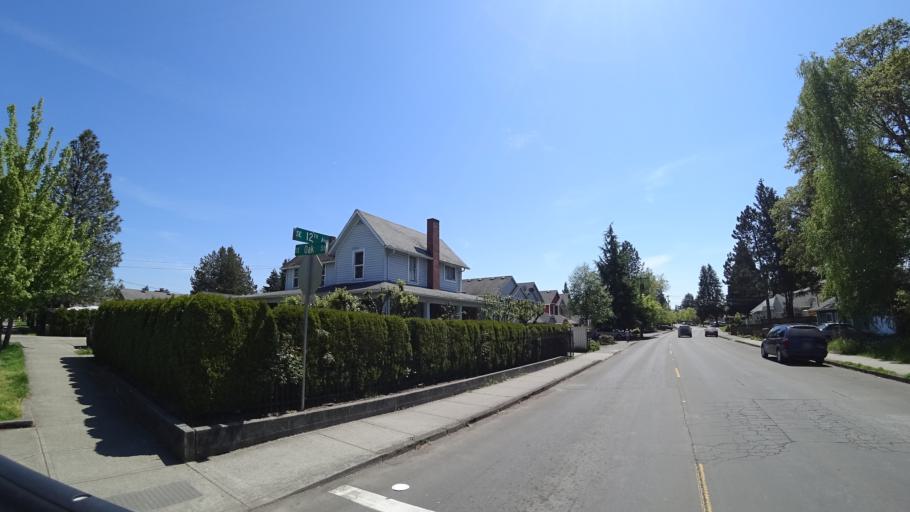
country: US
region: Oregon
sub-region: Washington County
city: Hillsboro
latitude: 45.5186
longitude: -122.9702
